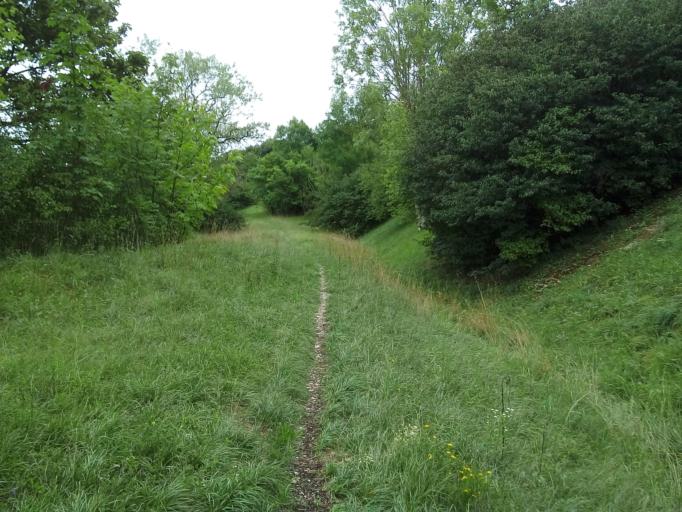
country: DE
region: Bavaria
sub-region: Upper Bavaria
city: Feldkirchen
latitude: 48.1491
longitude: 11.7129
